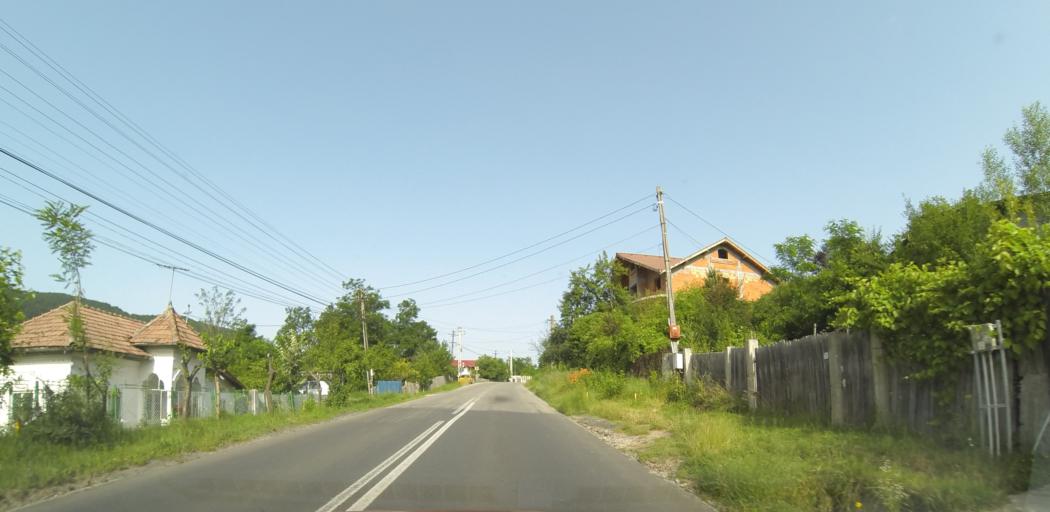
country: RO
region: Valcea
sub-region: Comuna Vladesti
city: Vladesti
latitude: 45.1219
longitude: 24.2930
